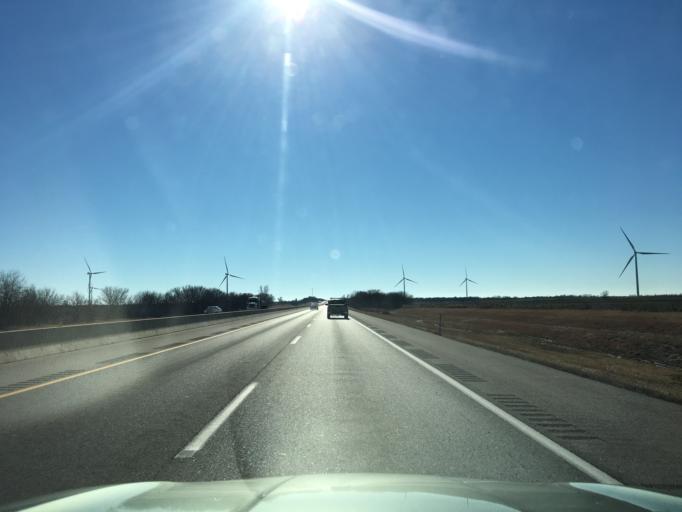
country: US
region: Kansas
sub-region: Sumner County
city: Wellington
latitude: 37.1422
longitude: -97.3394
